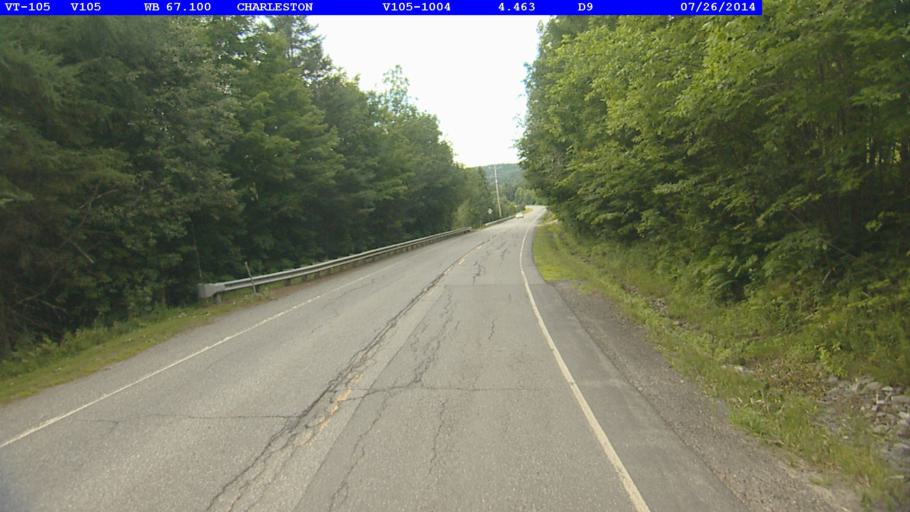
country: US
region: Vermont
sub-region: Orleans County
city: Newport
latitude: 44.8564
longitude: -72.0345
